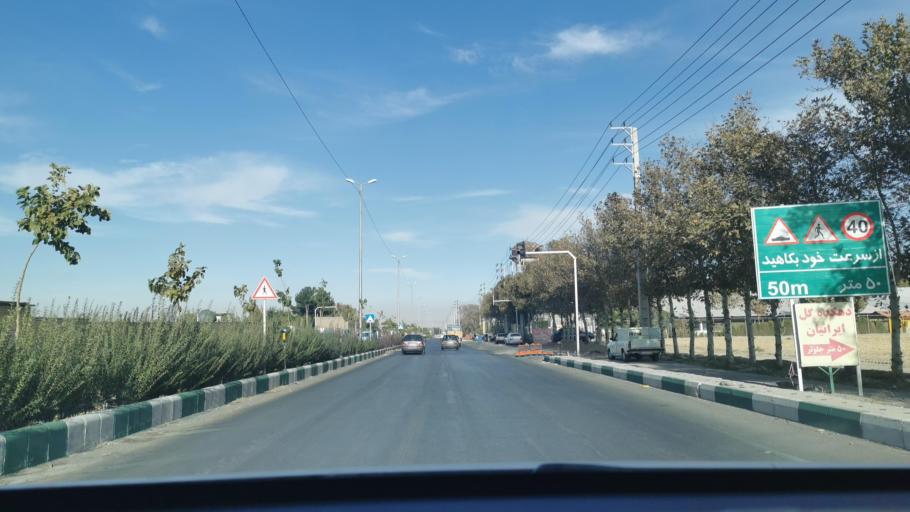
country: IR
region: Razavi Khorasan
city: Torqabeh
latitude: 36.4353
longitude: 59.4333
